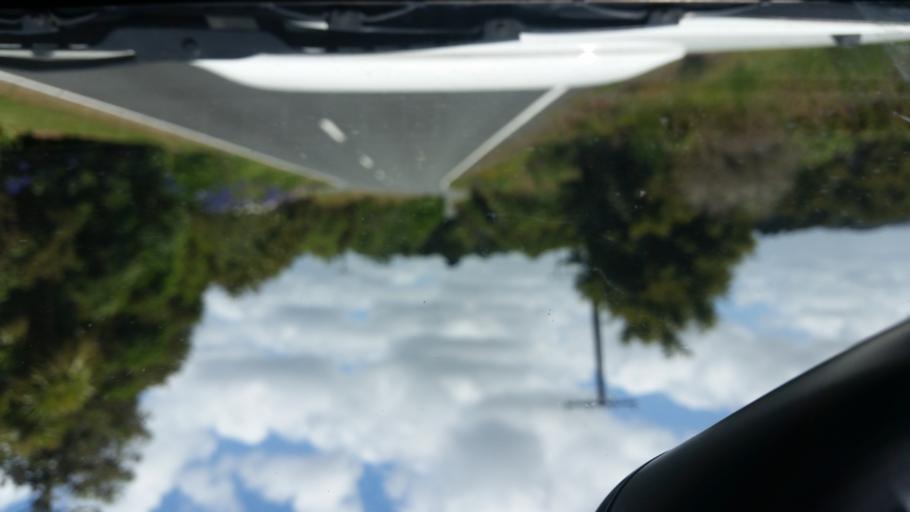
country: NZ
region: Northland
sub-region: Whangarei
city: Ruakaka
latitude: -36.0755
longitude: 174.2591
